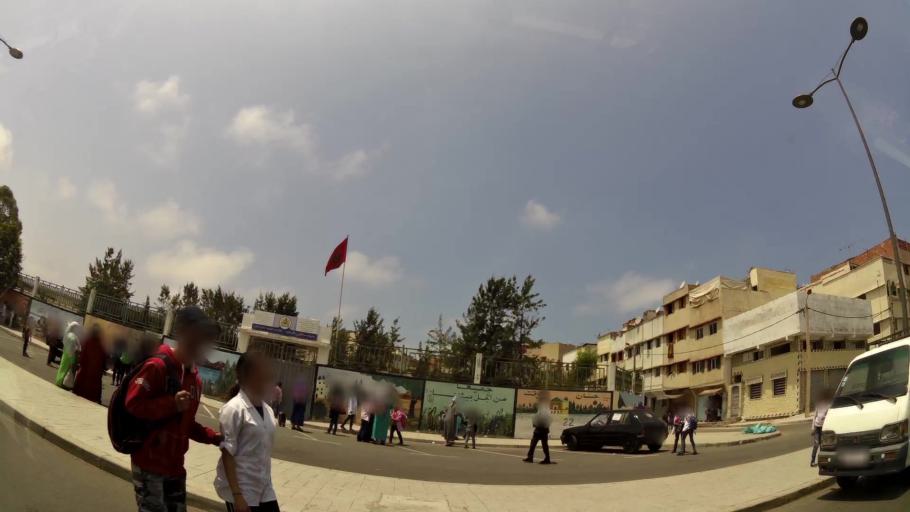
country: MA
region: Rabat-Sale-Zemmour-Zaer
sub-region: Rabat
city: Rabat
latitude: 33.9862
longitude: -6.8773
